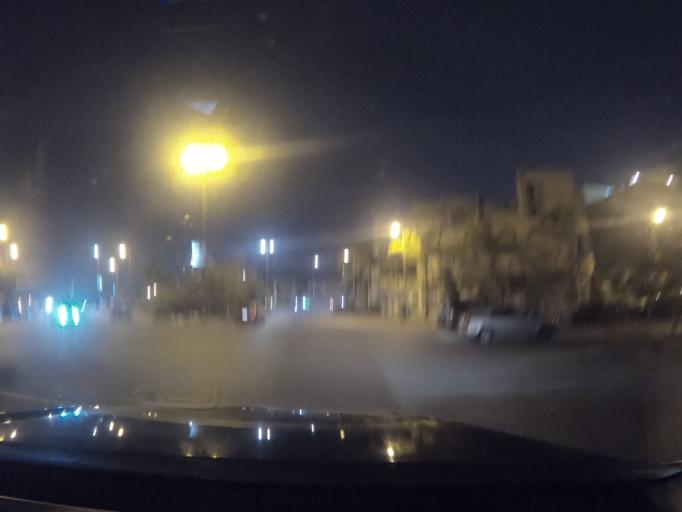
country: EG
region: Muhafazat al Qahirah
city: Cairo
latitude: 30.0110
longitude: 31.4154
